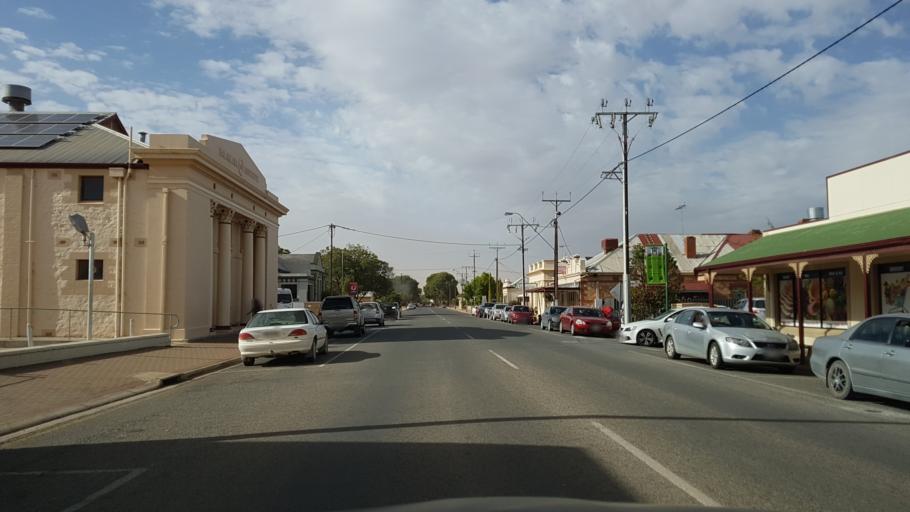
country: AU
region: South Australia
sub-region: Wakefield
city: Balaklava
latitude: -34.1464
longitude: 138.4152
